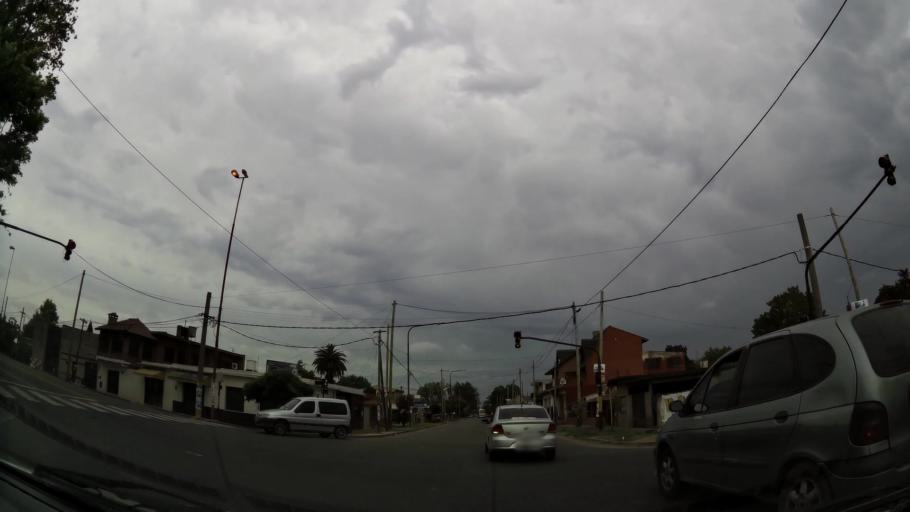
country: AR
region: Buenos Aires
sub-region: Partido de Quilmes
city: Quilmes
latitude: -34.7478
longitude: -58.2918
